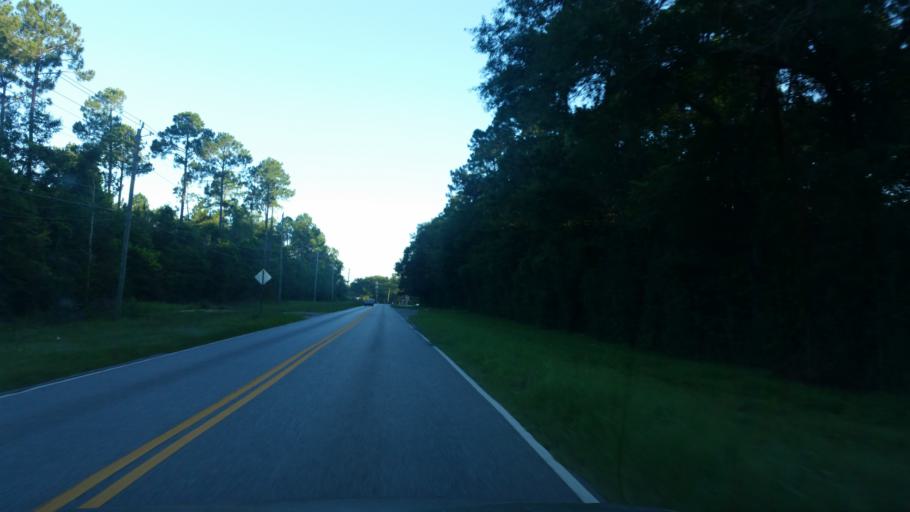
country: US
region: Florida
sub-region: Escambia County
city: Cantonment
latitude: 30.6012
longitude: -87.3290
